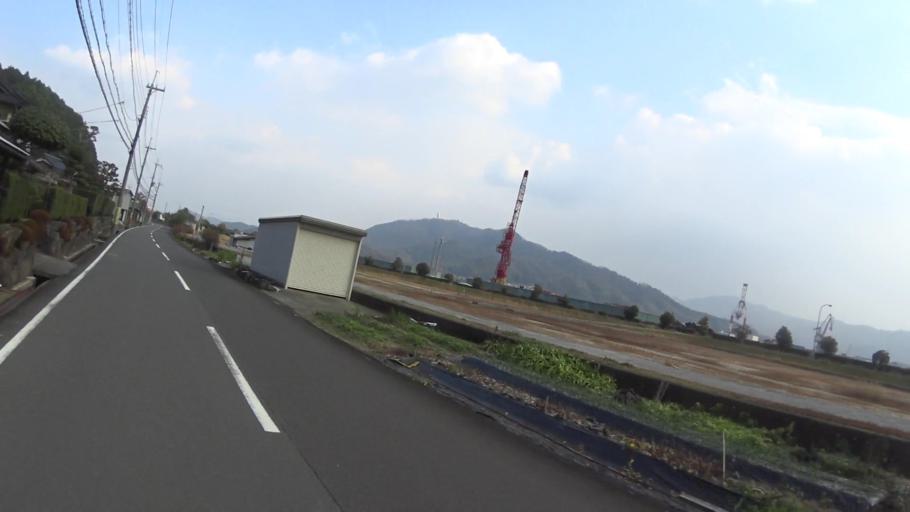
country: JP
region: Kyoto
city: Maizuru
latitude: 35.4601
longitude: 135.3130
